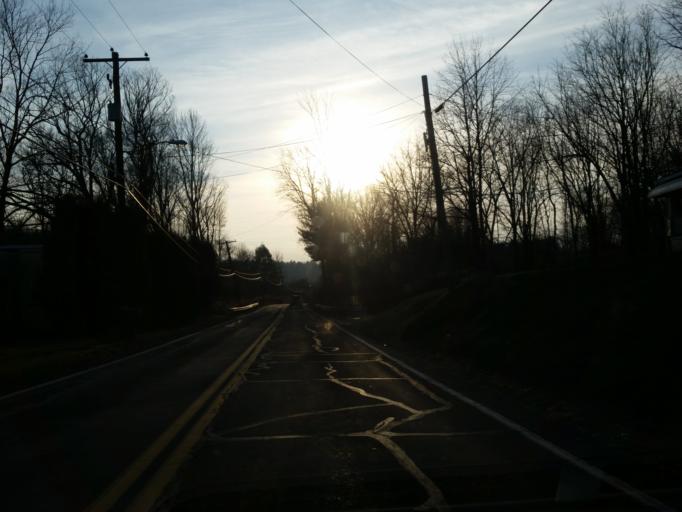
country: US
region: Pennsylvania
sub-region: Schuylkill County
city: Minersville
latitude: 40.6771
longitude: -76.2715
